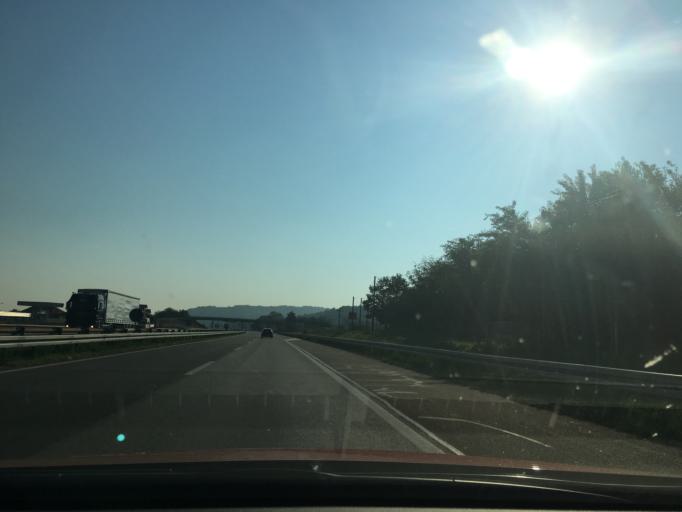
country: RS
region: Central Serbia
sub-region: Belgrade
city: Grocka
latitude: 44.5752
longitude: 20.7429
